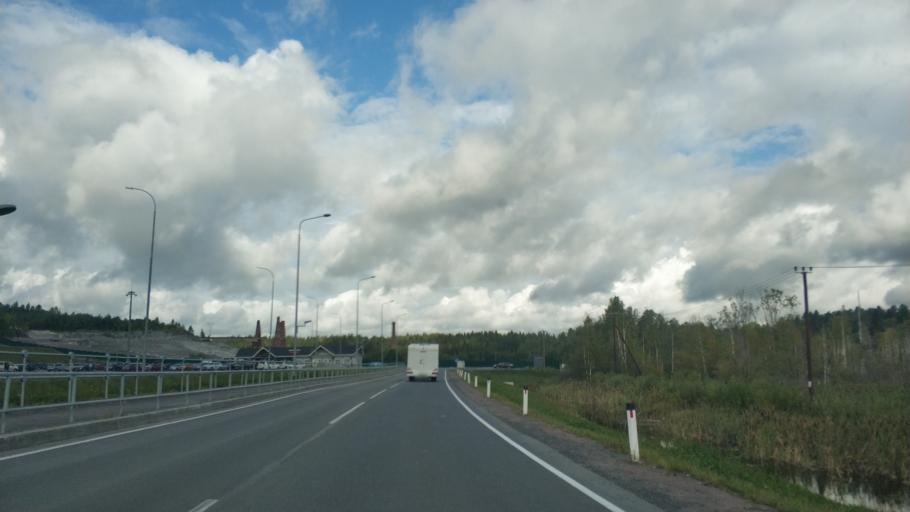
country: RU
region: Republic of Karelia
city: Ruskeala
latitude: 61.9483
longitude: 30.5872
